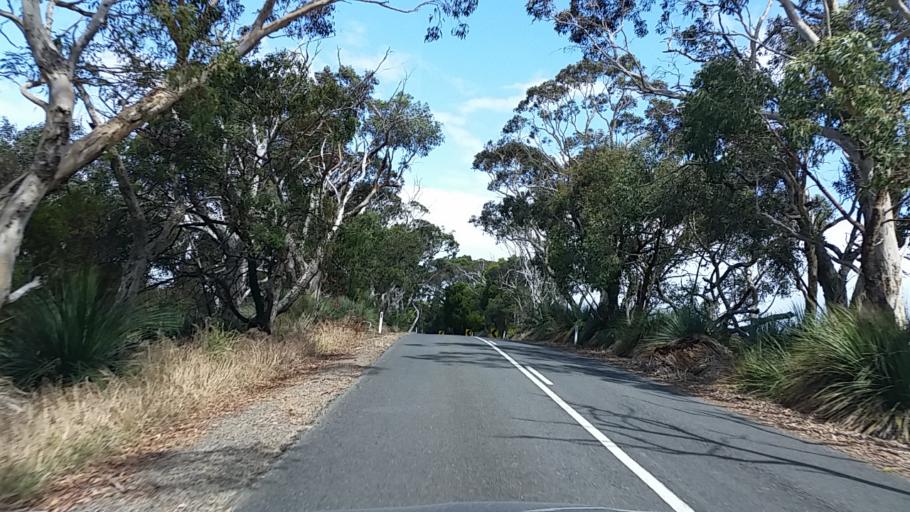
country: AU
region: South Australia
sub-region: Alexandrina
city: Port Elliot
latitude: -35.4650
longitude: 138.6549
